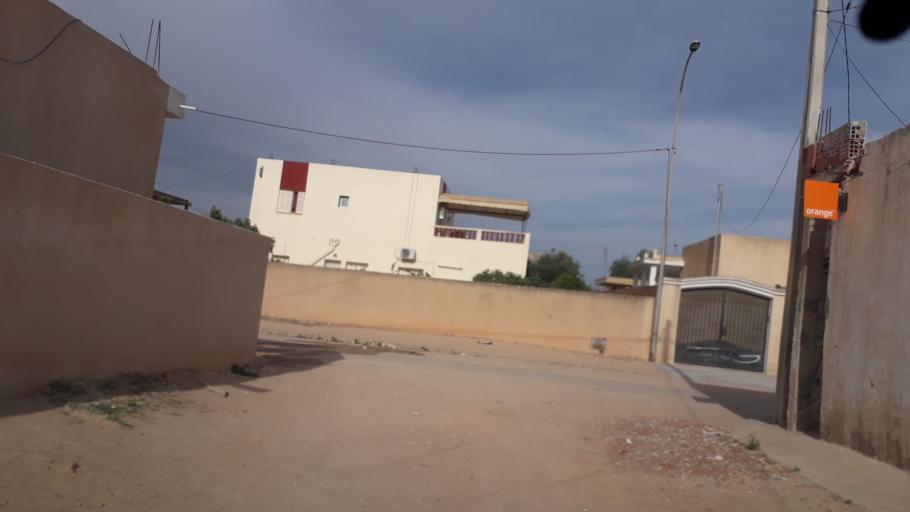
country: TN
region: Safaqis
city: Al Qarmadah
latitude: 34.8858
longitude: 10.7608
